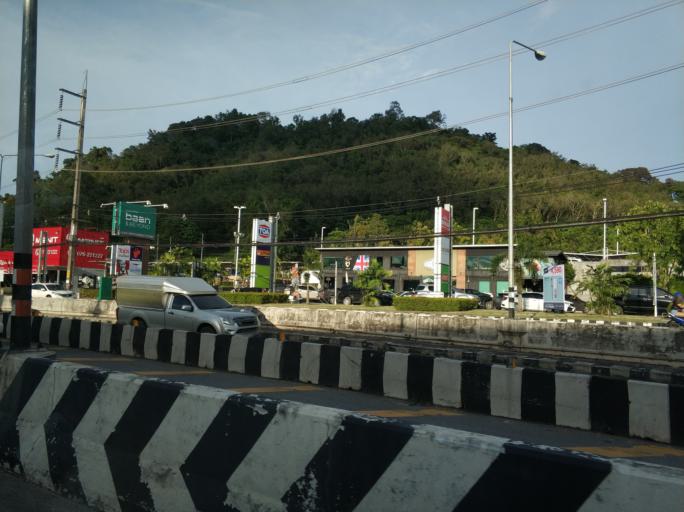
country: TH
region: Phuket
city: Wichit
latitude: 7.8927
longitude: 98.3690
